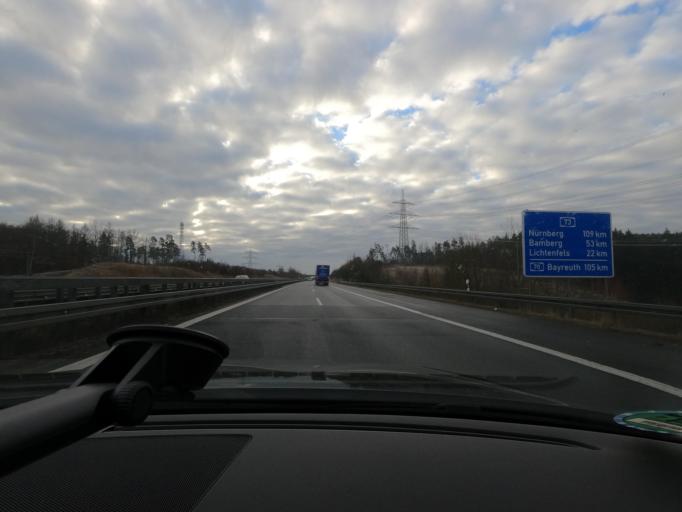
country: DE
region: Bavaria
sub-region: Upper Franconia
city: Rodental
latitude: 50.2767
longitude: 11.0163
